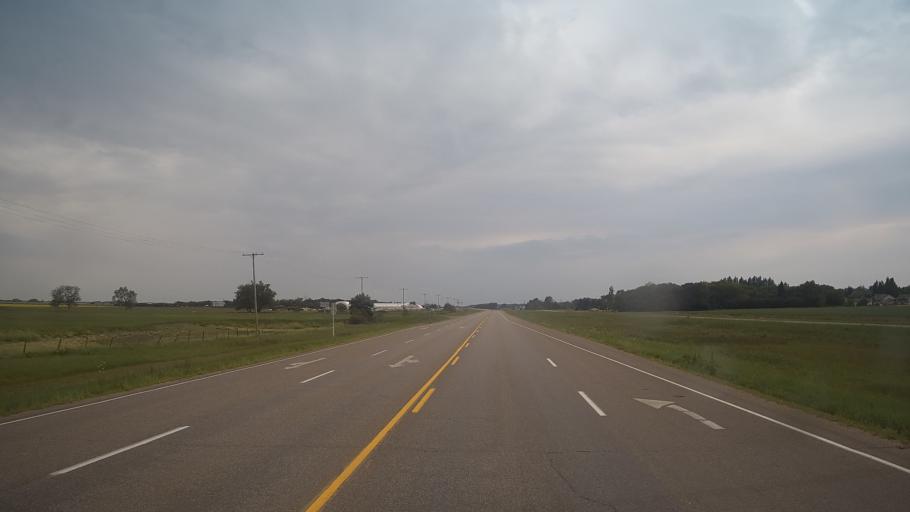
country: CA
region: Saskatchewan
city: Langham
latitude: 52.1289
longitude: -107.2180
